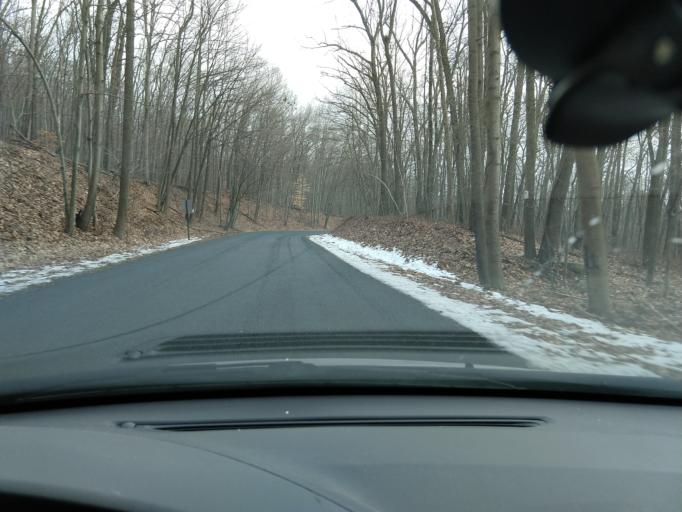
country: US
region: Pennsylvania
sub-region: Chester County
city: Elverson
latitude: 40.1924
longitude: -75.7831
